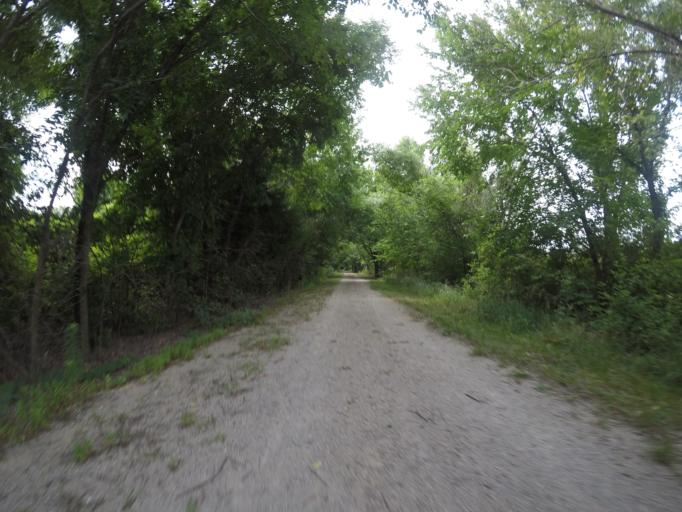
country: US
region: Kansas
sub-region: Anderson County
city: Garnett
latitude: 38.4113
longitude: -95.2615
